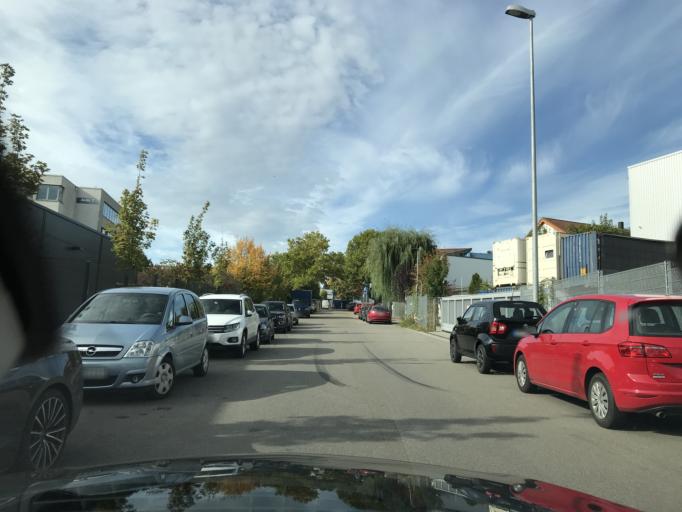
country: DE
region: Baden-Wuerttemberg
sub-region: Regierungsbezirk Stuttgart
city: Waiblingen
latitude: 48.8224
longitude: 9.3251
